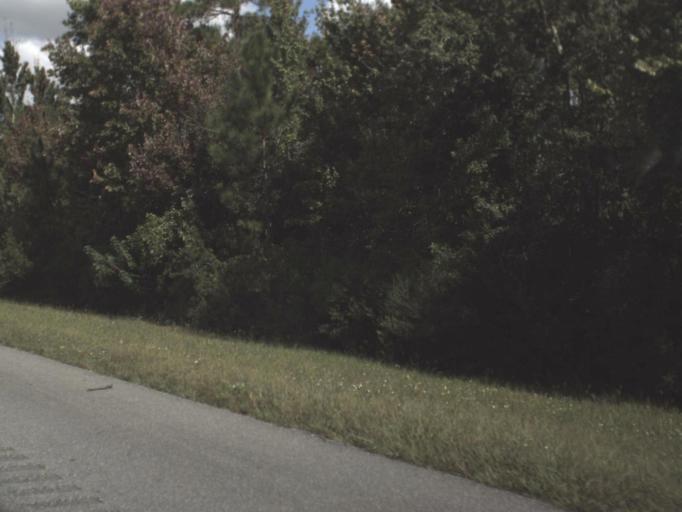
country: US
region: Florida
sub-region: Osceola County
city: Buenaventura Lakes
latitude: 28.3320
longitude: -81.3766
